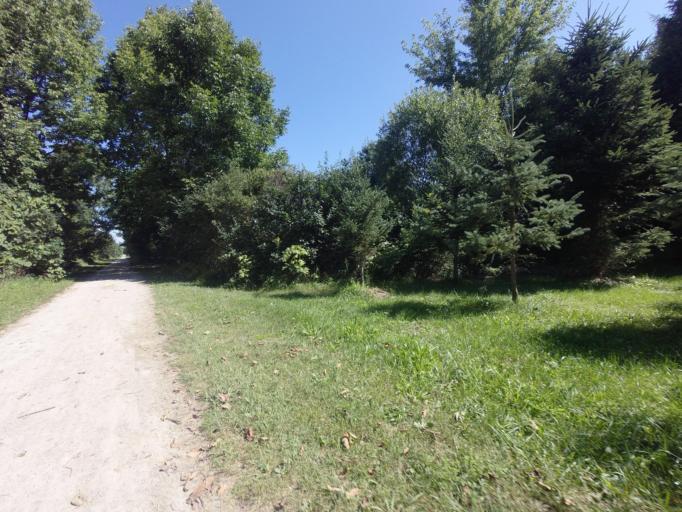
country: CA
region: Ontario
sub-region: Wellington County
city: Guelph
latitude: 43.7274
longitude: -80.3704
